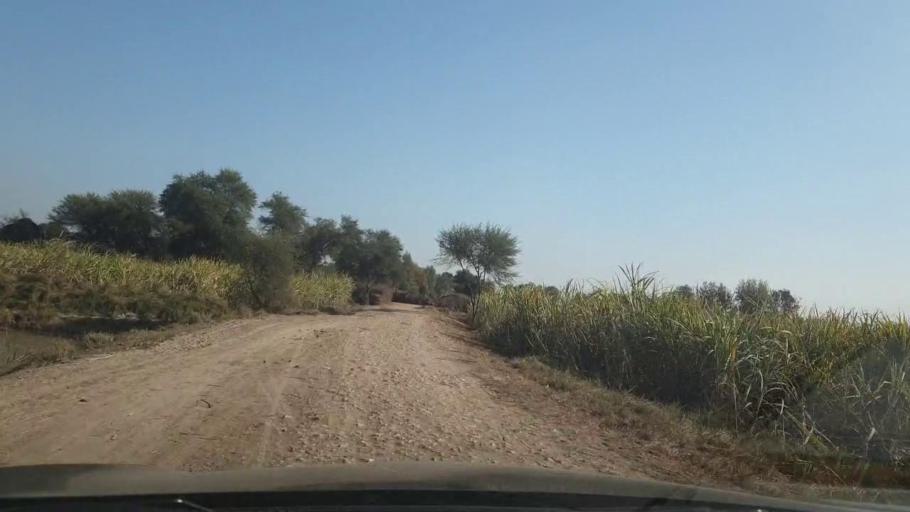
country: PK
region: Sindh
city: Khairpur
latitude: 28.1349
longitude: 69.6057
